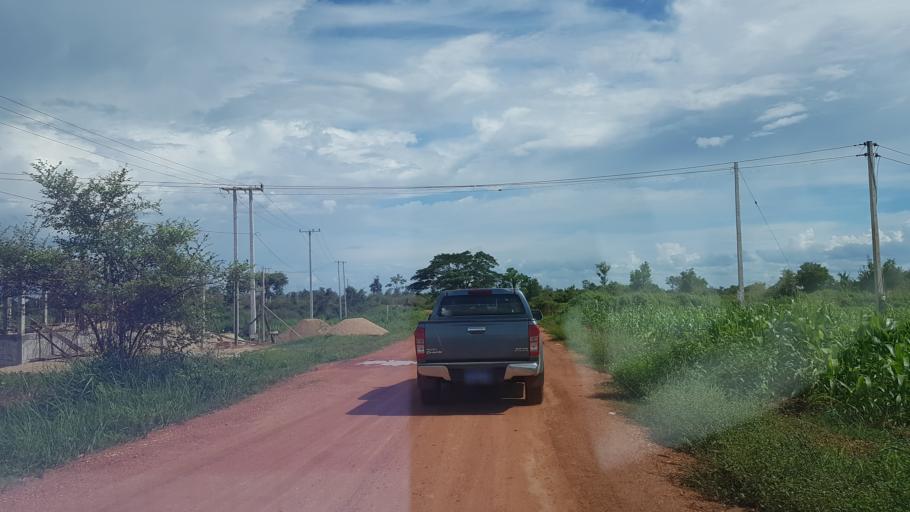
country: LA
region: Vientiane
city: Vientiane
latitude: 18.2103
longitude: 102.5659
